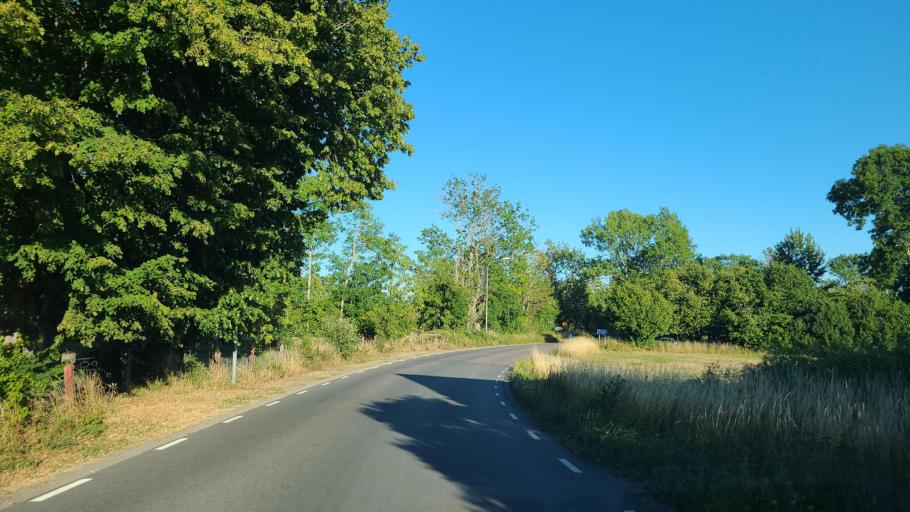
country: SE
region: Kalmar
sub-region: Oskarshamns Kommun
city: Oskarshamn
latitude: 57.3222
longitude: 17.0133
